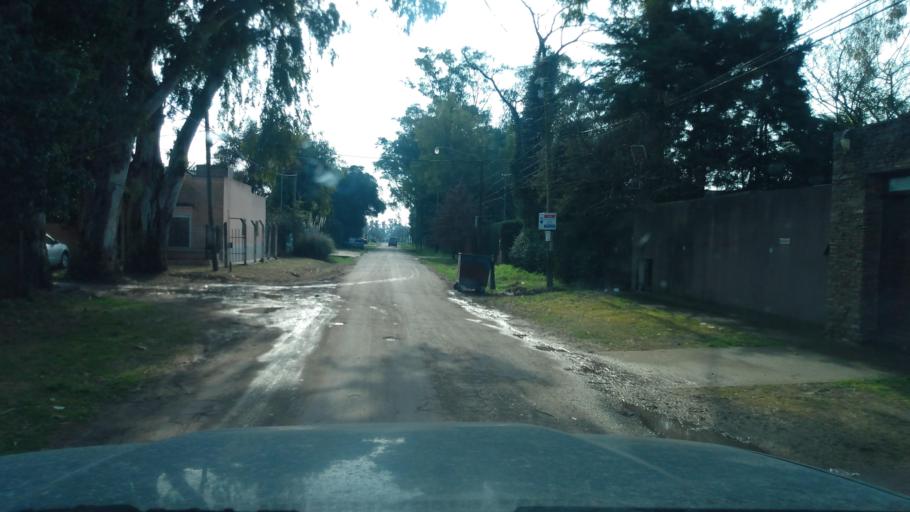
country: AR
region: Buenos Aires
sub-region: Partido de Lujan
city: Lujan
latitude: -34.5715
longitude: -59.0866
